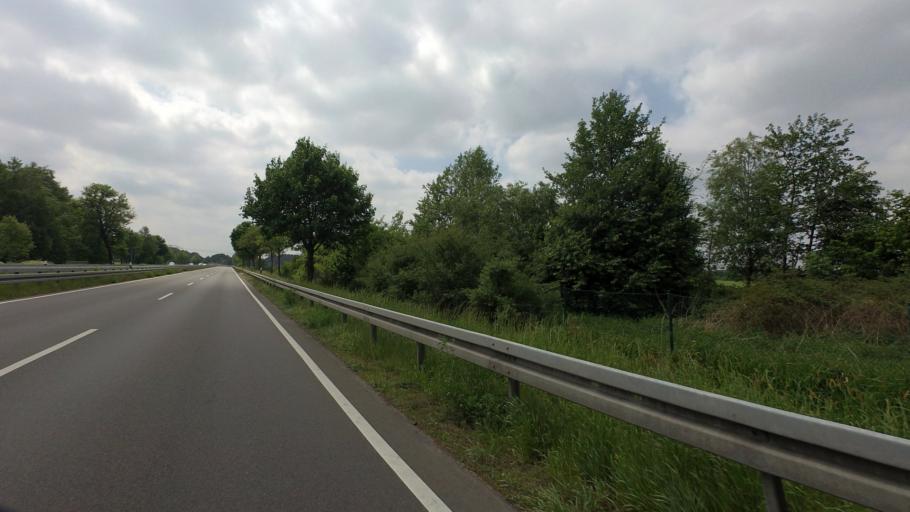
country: DE
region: Brandenburg
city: Peitz
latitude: 51.8247
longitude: 14.3866
